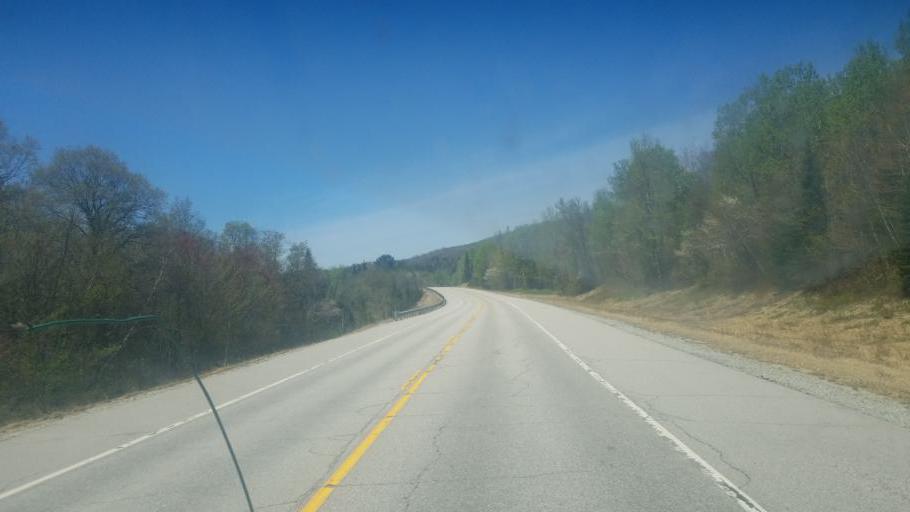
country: US
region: New Hampshire
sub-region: Grafton County
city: Deerfield
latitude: 44.2693
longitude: -71.5069
